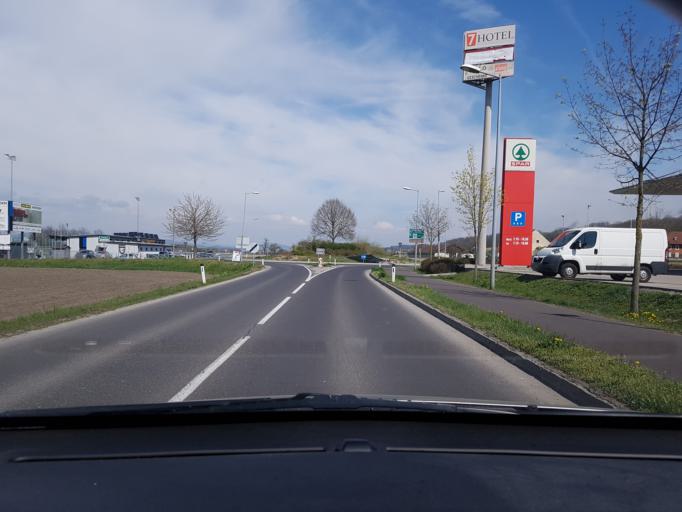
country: AT
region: Upper Austria
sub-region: Politischer Bezirk Linz-Land
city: Ansfelden
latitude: 48.2125
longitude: 14.2872
